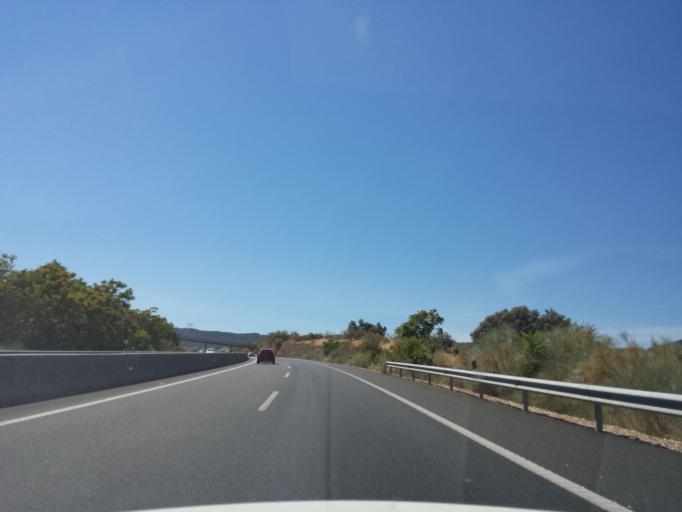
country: ES
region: Extremadura
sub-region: Provincia de Caceres
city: Casas de Miravete
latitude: 39.7466
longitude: -5.7267
